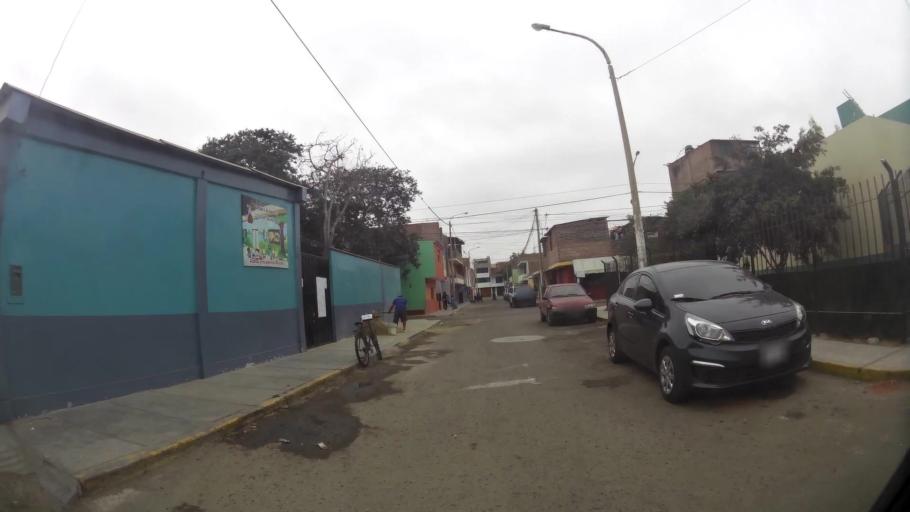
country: PE
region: La Libertad
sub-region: Provincia de Trujillo
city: Trujillo
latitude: -8.1074
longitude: -79.0396
